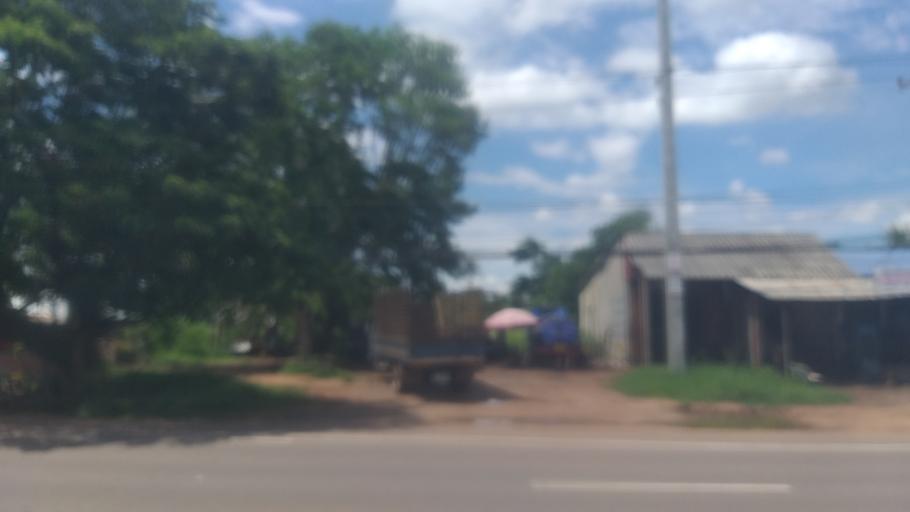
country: TH
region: Nakhon Ratchasima
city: Phra Thong Kham
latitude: 15.3089
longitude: 101.9686
